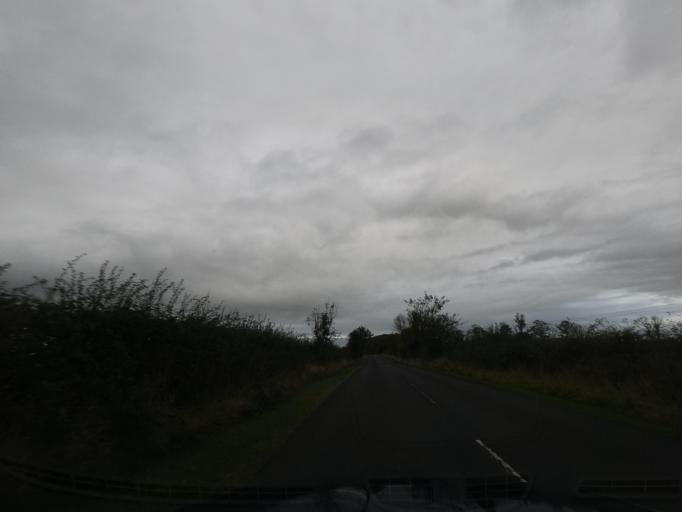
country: GB
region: England
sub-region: Northumberland
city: Ford
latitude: 55.6878
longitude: -2.0843
